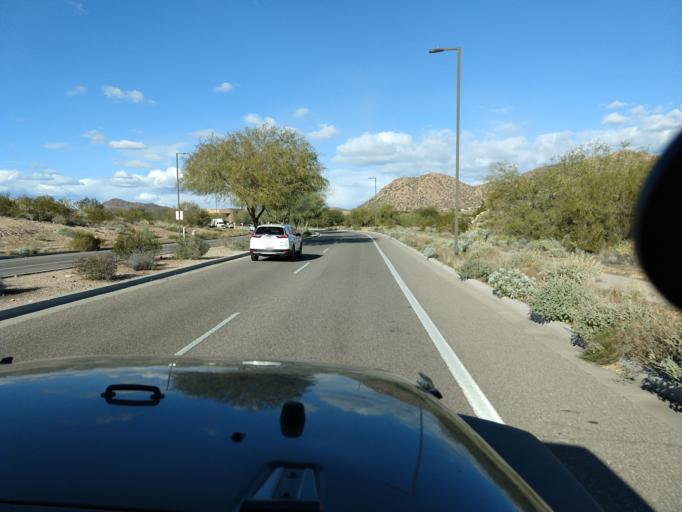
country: US
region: Arizona
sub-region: Maricopa County
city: Anthem
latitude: 33.7933
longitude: -112.1171
